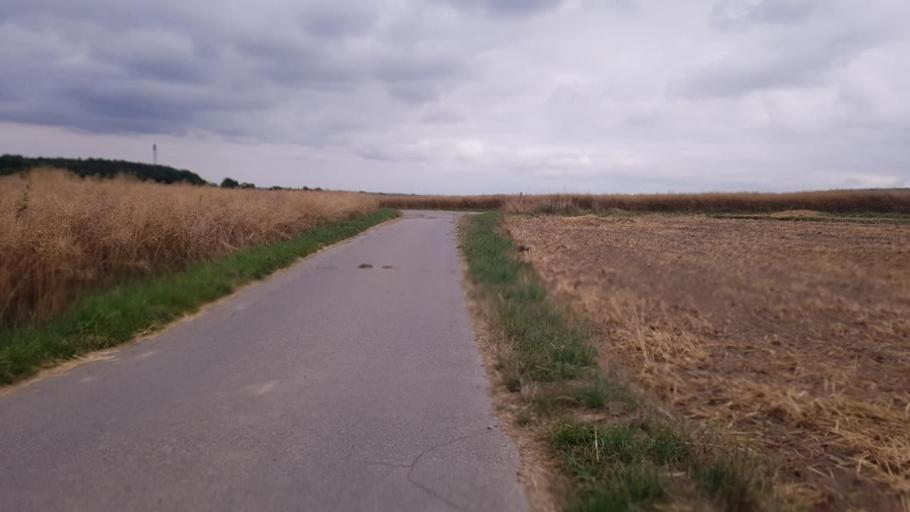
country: DE
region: North Rhine-Westphalia
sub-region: Regierungsbezirk Koln
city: Kreuzau
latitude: 50.7358
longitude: 6.4387
